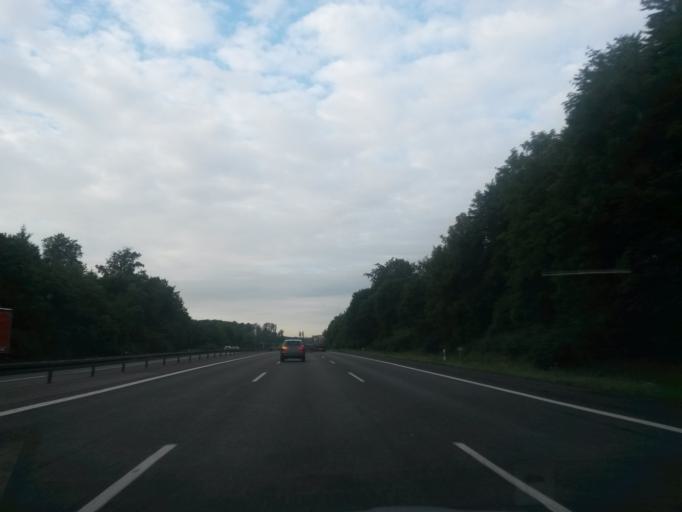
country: DE
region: Bavaria
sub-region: Upper Bavaria
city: Denkendorf
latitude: 48.9095
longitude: 11.4701
